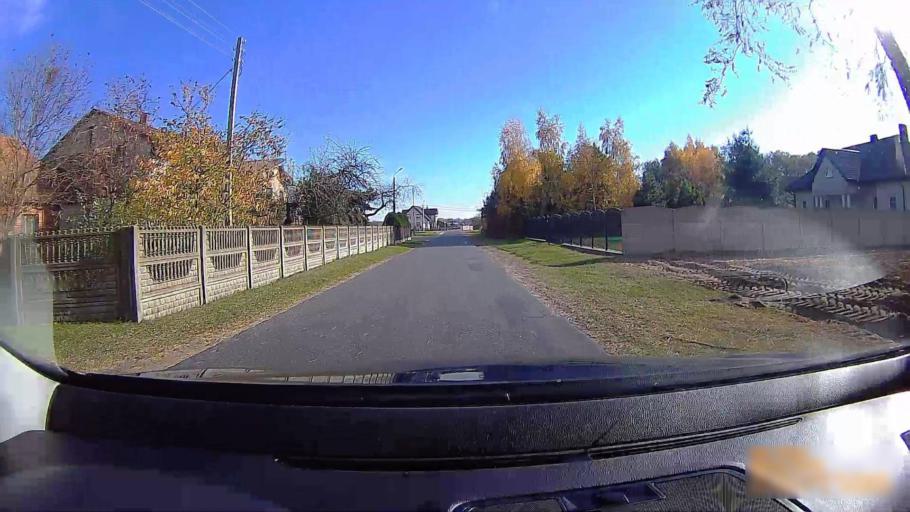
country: PL
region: Greater Poland Voivodeship
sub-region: Powiat ostrzeszowski
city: Doruchow
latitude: 51.3921
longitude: 18.0528
